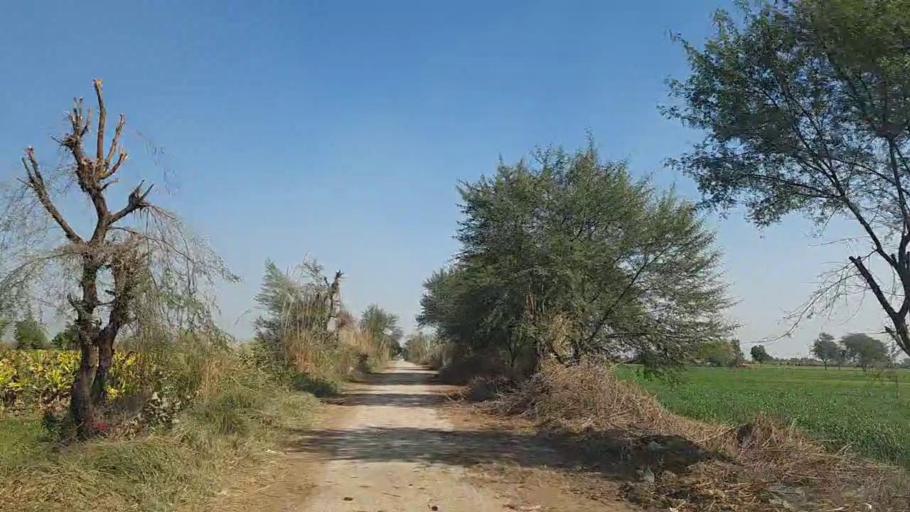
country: PK
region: Sindh
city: Jam Sahib
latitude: 26.2233
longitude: 68.6050
